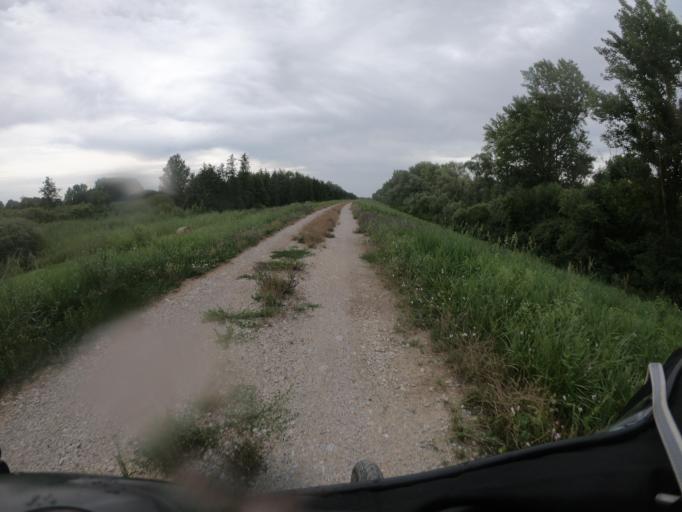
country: HU
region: Jasz-Nagykun-Szolnok
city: Tiszafured
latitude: 47.6786
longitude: 20.7666
